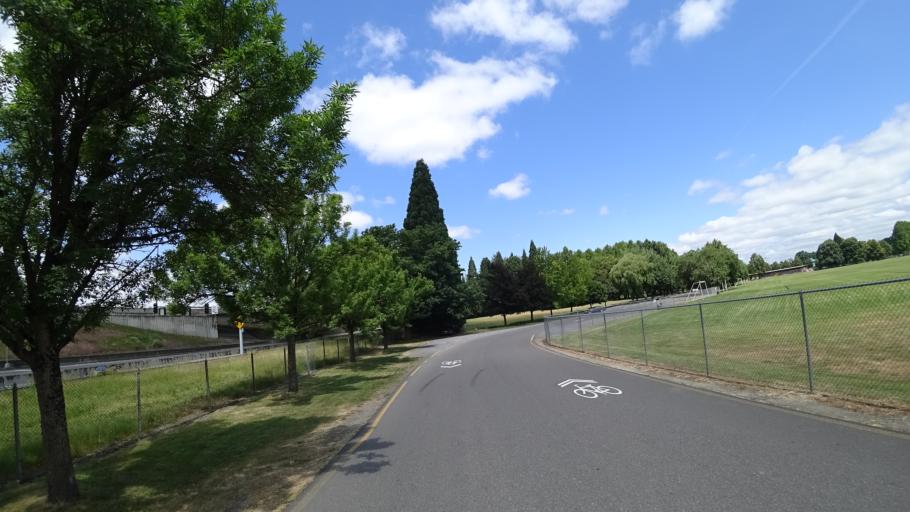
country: US
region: Washington
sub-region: Clark County
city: Vancouver
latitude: 45.5961
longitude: -122.6833
